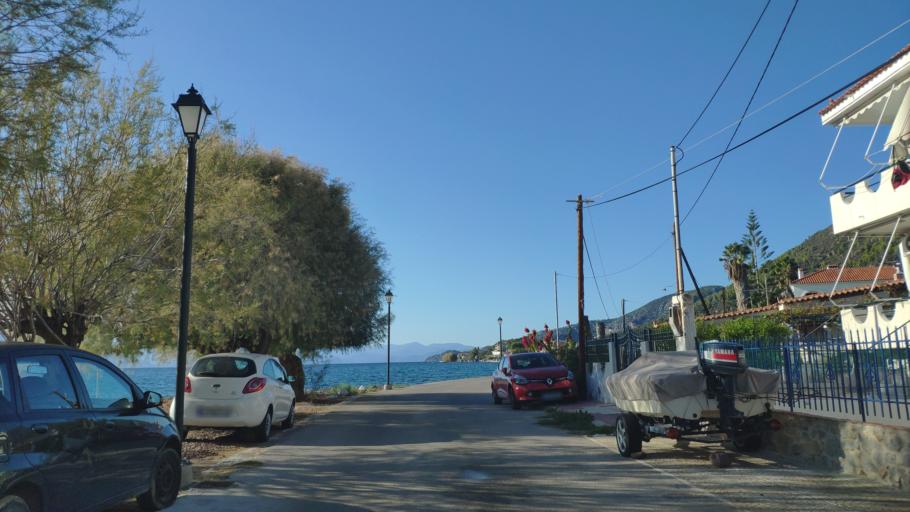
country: GR
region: Attica
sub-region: Nomos Piraios
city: Megalochori
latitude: 37.5870
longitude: 23.3471
